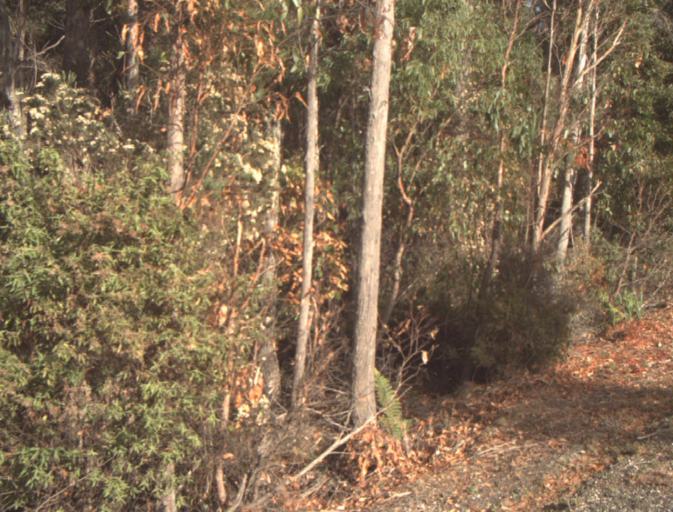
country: AU
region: Tasmania
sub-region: Dorset
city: Bridport
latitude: -41.1688
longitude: 147.2627
